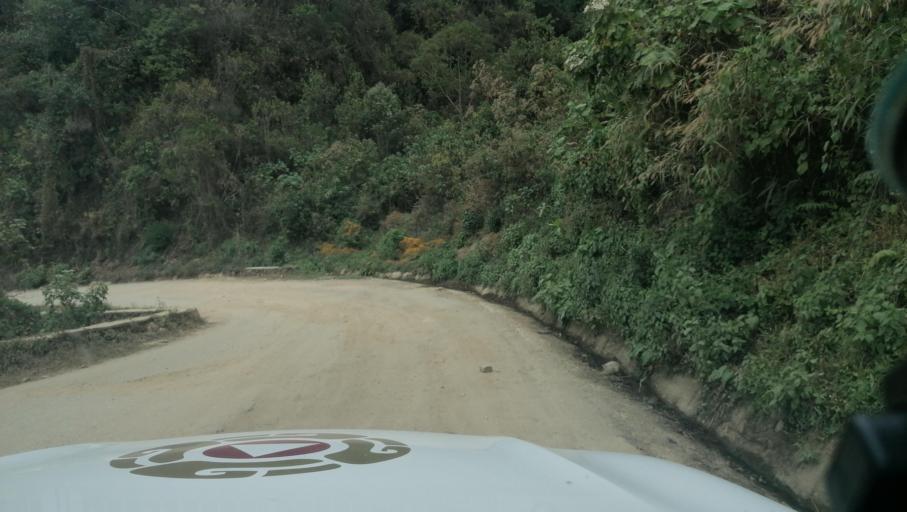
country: GT
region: San Marcos
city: Tacana
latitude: 15.2092
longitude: -92.1940
